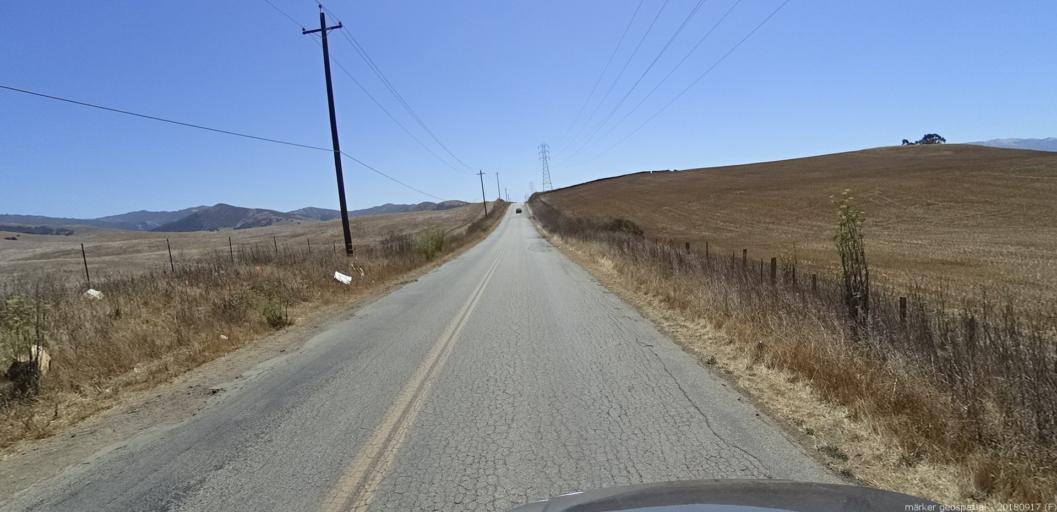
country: US
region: California
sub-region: Monterey County
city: Salinas
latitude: 36.7105
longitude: -121.5852
